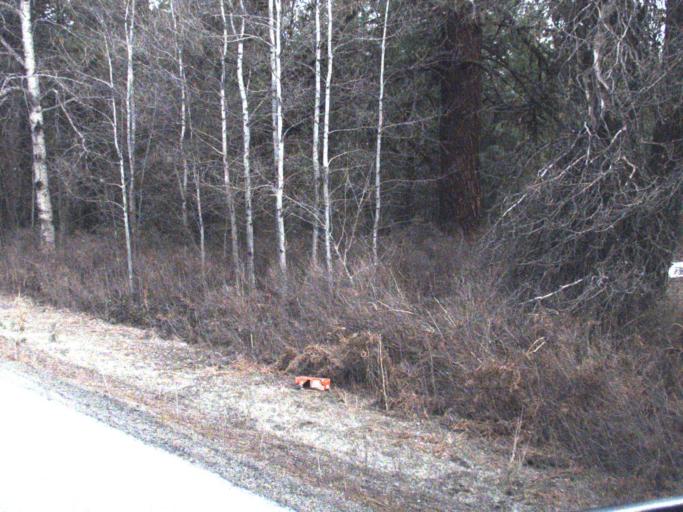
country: US
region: Washington
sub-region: Pend Oreille County
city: Newport
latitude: 48.2264
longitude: -117.1376
